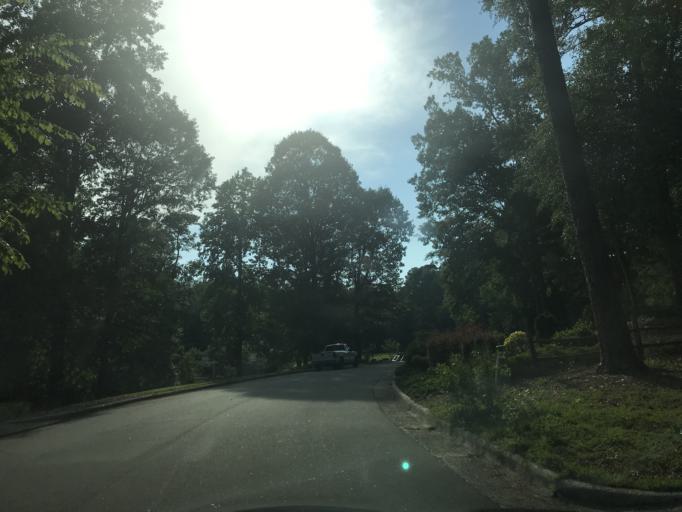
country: US
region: North Carolina
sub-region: Wake County
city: Knightdale
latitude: 35.8286
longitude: -78.5447
